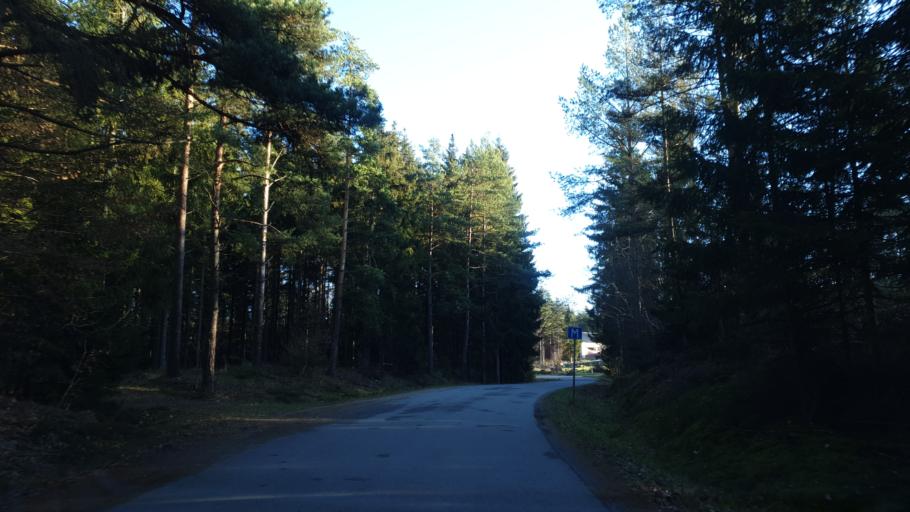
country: SE
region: Blekinge
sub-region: Ronneby Kommun
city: Brakne-Hoby
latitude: 56.2312
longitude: 15.1623
